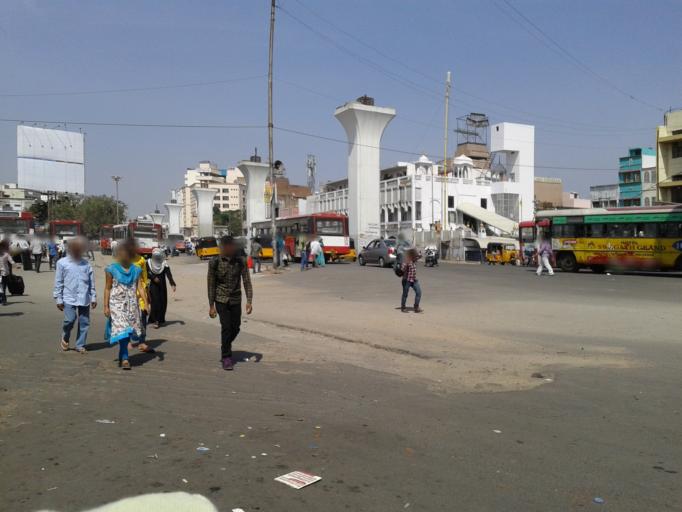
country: IN
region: Telangana
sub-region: Hyderabad
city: Malkajgiri
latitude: 17.4355
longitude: 78.5004
